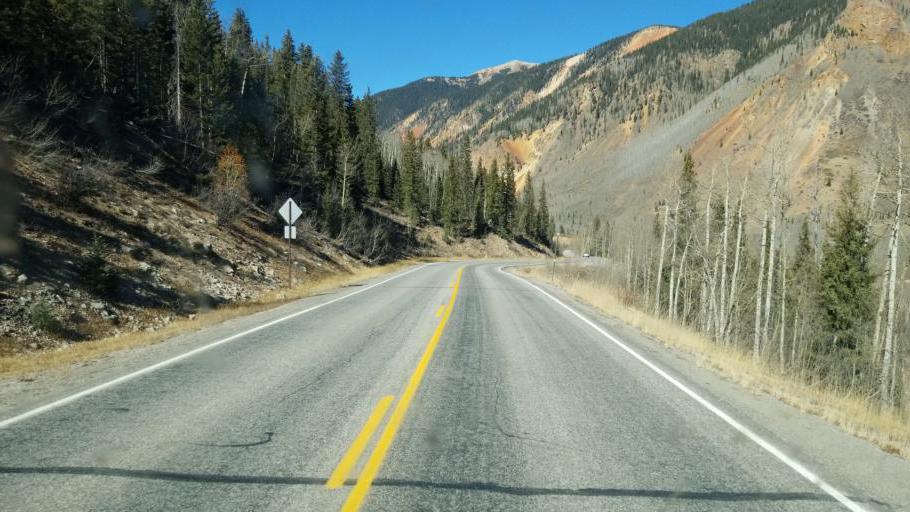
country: US
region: Colorado
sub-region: San Juan County
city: Silverton
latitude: 37.8013
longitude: -107.6767
